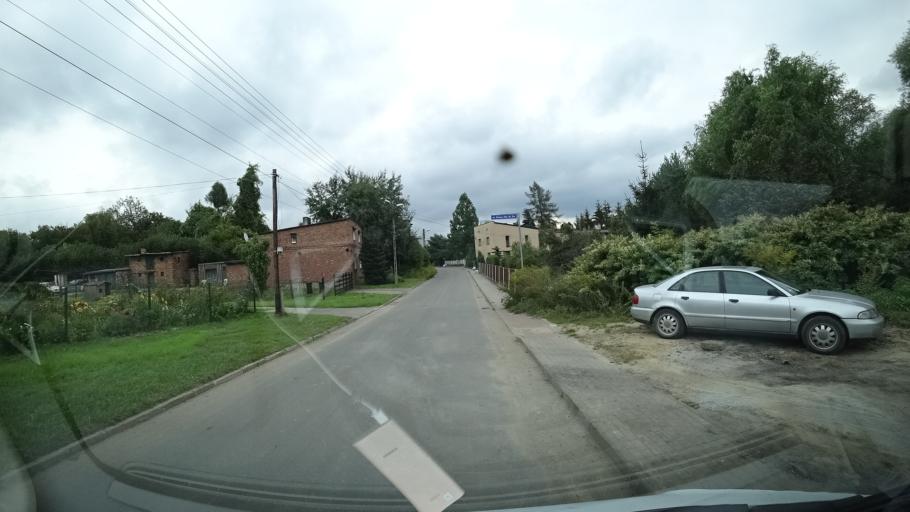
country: PL
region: Silesian Voivodeship
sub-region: Ruda Slaska
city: Ruda Slaska
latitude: 50.2665
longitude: 18.8183
